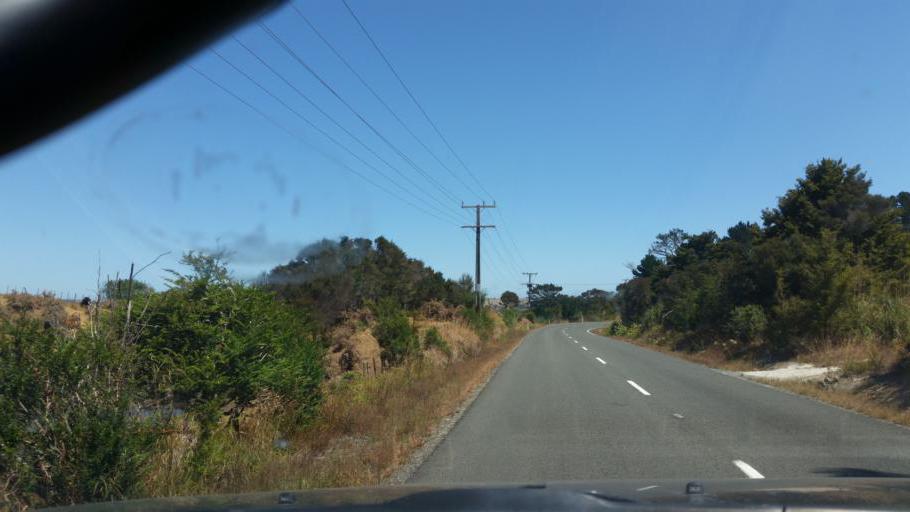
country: NZ
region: Northland
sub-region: Kaipara District
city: Dargaville
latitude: -36.0084
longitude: 173.9449
